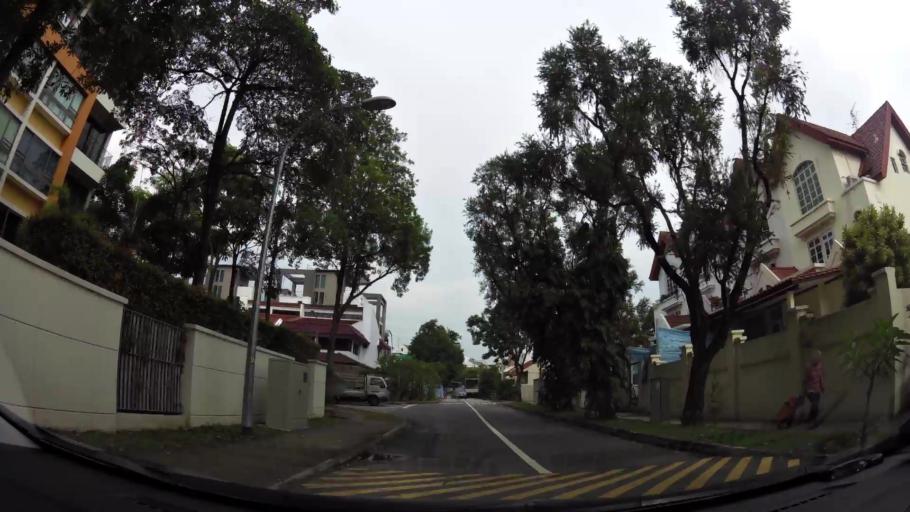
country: SG
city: Singapore
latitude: 1.3495
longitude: 103.8810
